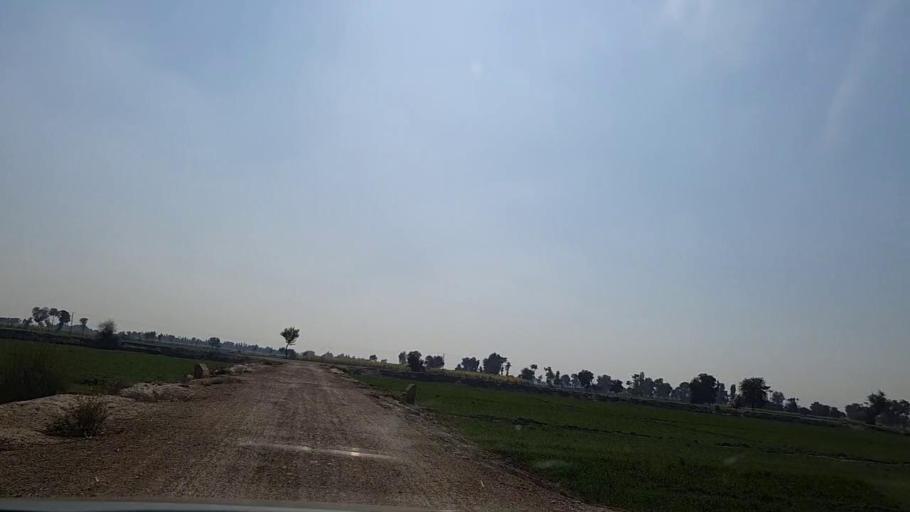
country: PK
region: Sindh
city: Daulatpur
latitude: 26.2857
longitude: 68.0537
